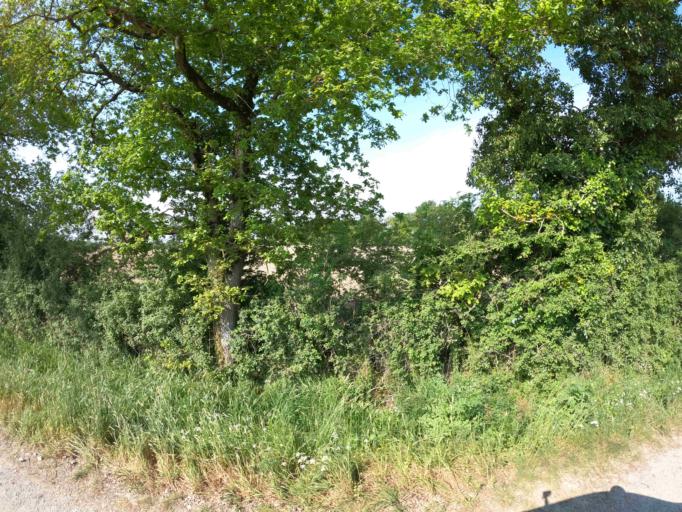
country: FR
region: Pays de la Loire
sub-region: Departement de la Vendee
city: Treize-Septiers
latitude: 47.0051
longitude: -1.2500
